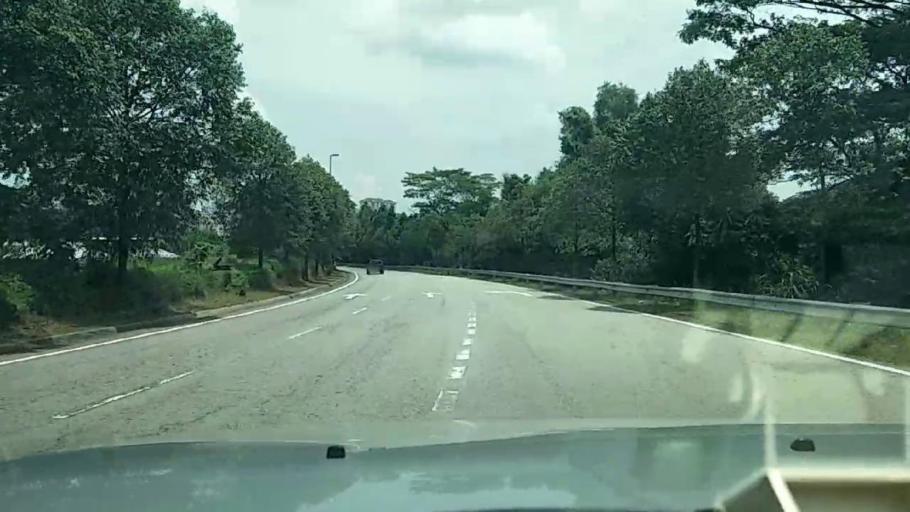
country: MY
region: Kuala Lumpur
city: Kuala Lumpur
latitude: 3.0934
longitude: 101.6945
